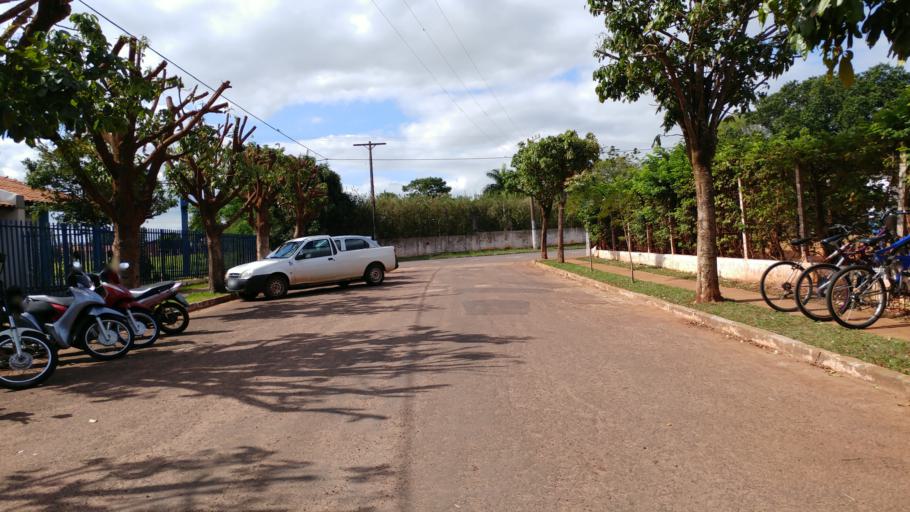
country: BR
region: Sao Paulo
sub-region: Paraguacu Paulista
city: Paraguacu Paulista
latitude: -22.4181
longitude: -50.5886
